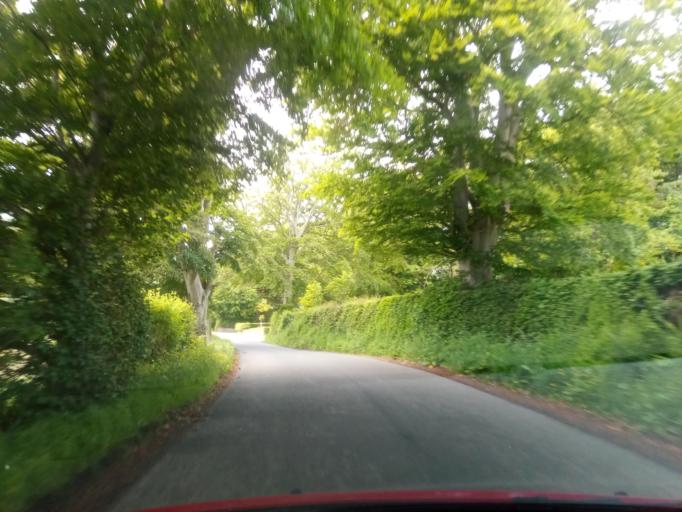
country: GB
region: Scotland
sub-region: The Scottish Borders
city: Selkirk
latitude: 55.5858
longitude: -2.8473
